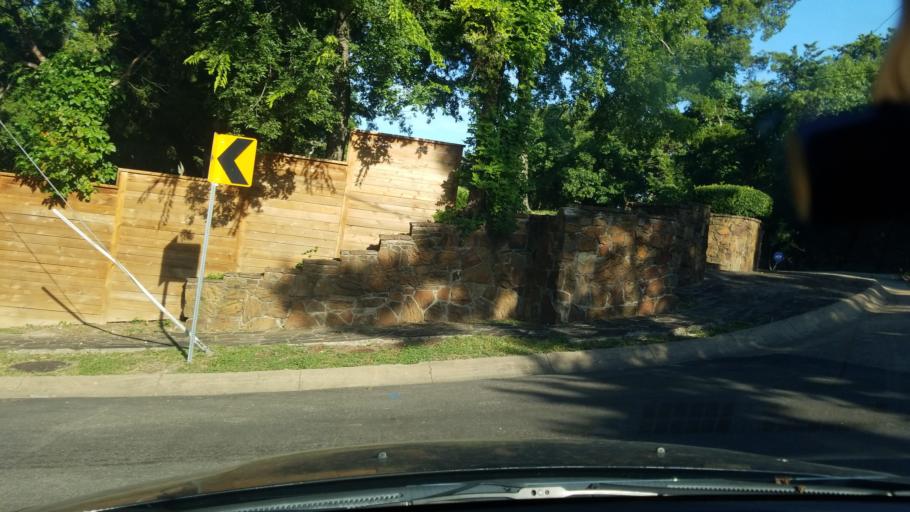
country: US
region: Texas
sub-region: Dallas County
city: Dallas
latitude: 32.7314
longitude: -96.8200
